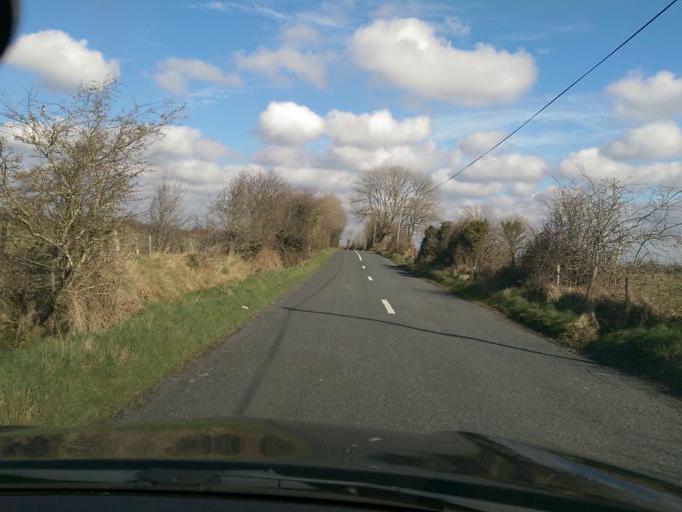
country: IE
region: Connaught
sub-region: County Galway
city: Athenry
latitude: 53.4445
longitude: -8.5607
